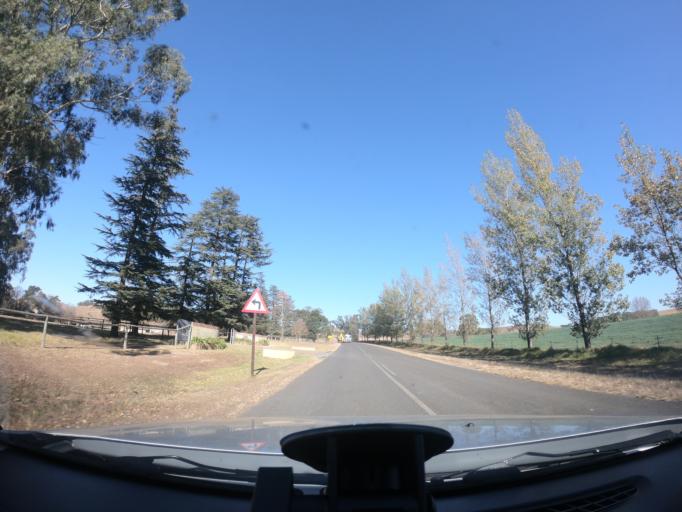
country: ZA
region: KwaZulu-Natal
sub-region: uMgungundlovu District Municipality
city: Mooirivier
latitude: -29.3164
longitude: 29.9227
